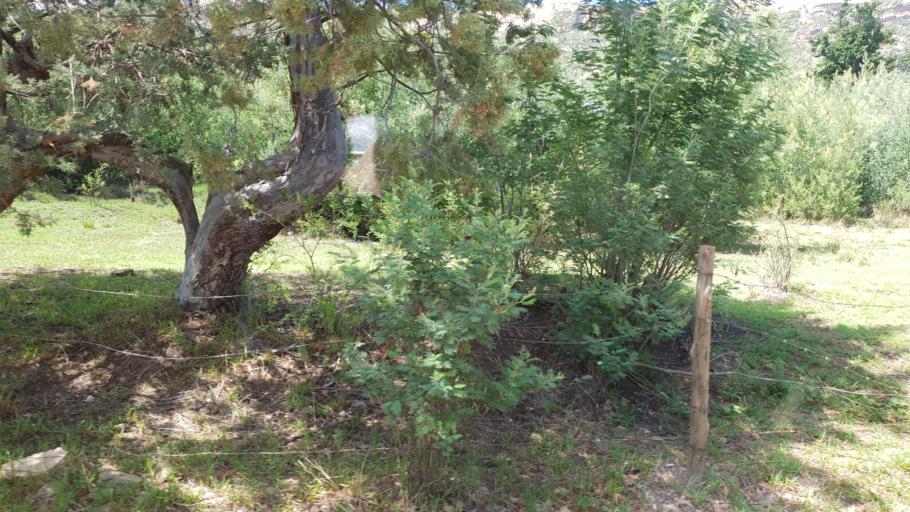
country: LS
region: Maseru
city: Nako
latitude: -29.6296
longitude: 27.5044
